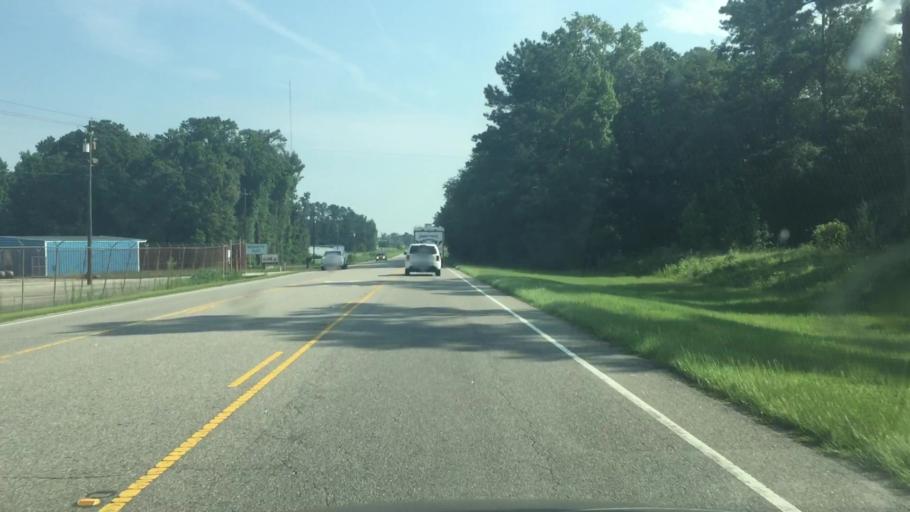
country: US
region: North Carolina
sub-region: Columbus County
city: Tabor City
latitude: 34.1469
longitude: -78.8630
